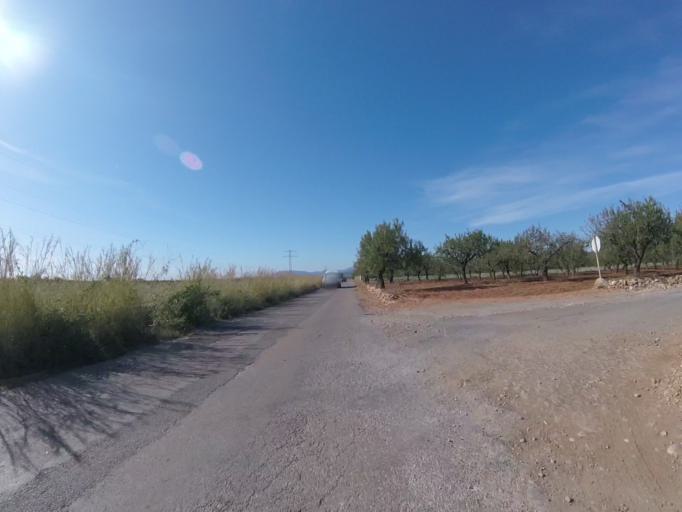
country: ES
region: Valencia
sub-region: Provincia de Castello
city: Torreblanca
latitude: 40.2149
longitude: 0.2162
